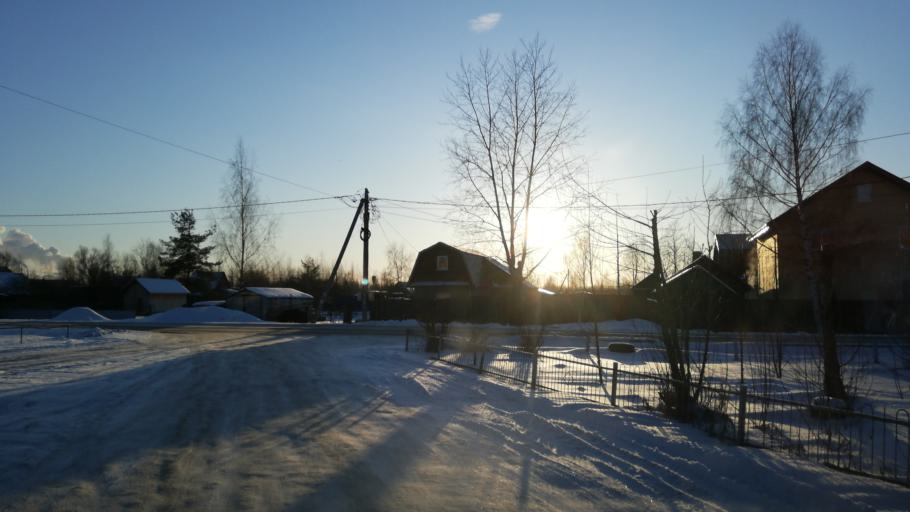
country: RU
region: Jaroslavl
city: Yaroslavl
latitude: 57.6152
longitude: 39.7898
